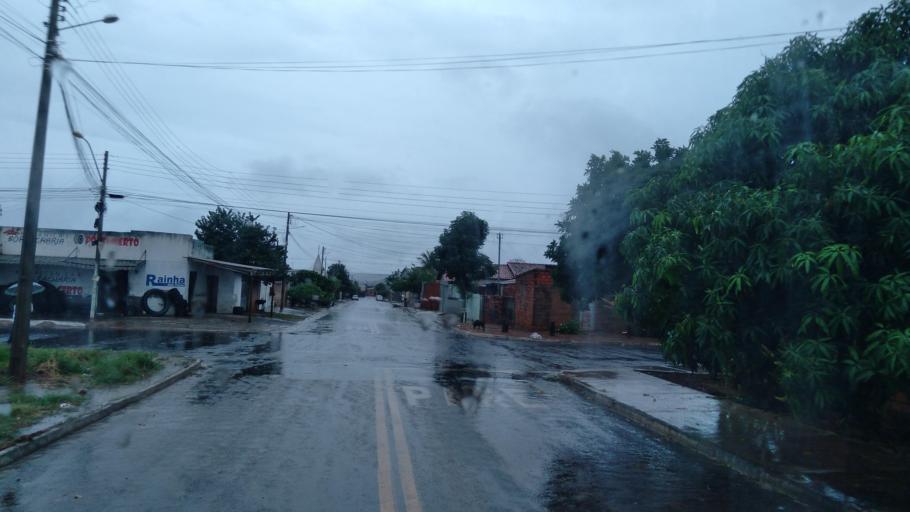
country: BR
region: Goias
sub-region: Mineiros
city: Mineiros
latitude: -17.5413
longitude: -52.5423
